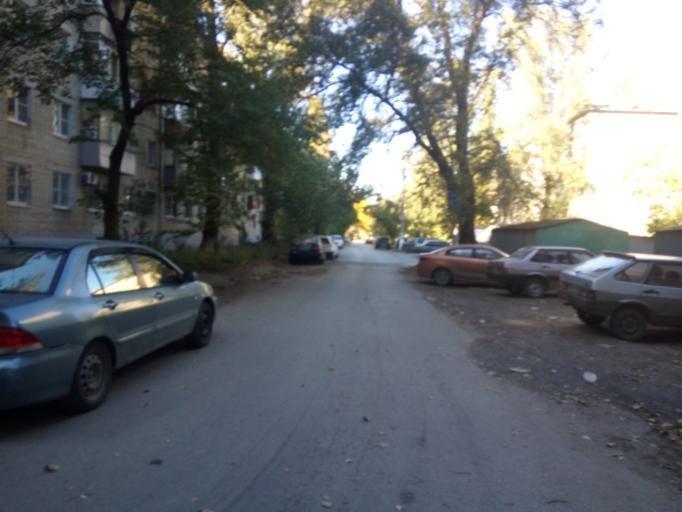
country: RU
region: Rostov
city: Bataysk
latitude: 47.1226
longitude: 39.7339
